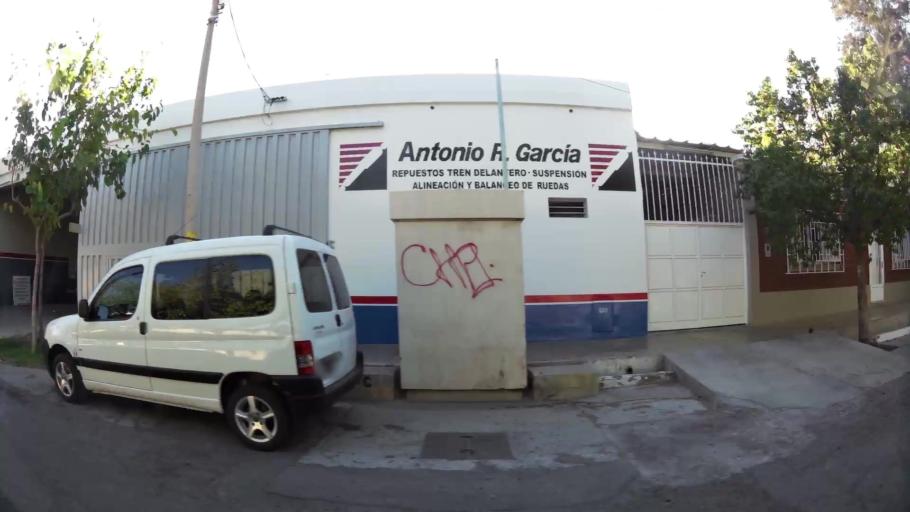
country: AR
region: San Juan
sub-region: Departamento de Santa Lucia
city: Santa Lucia
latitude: -31.5359
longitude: -68.5066
